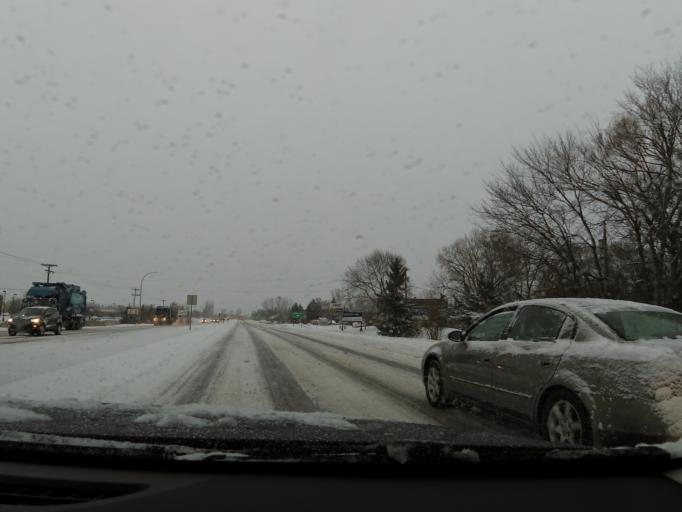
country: US
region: Minnesota
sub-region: Hennepin County
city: Eden Prairie
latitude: 44.8394
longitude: -93.4408
